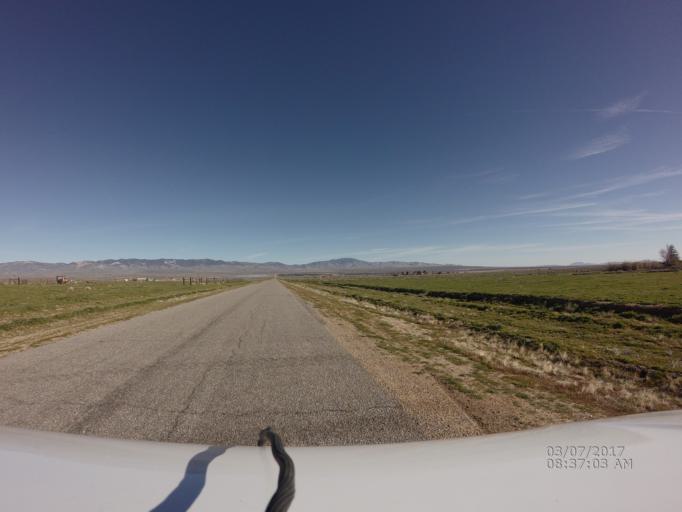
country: US
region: California
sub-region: Los Angeles County
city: Green Valley
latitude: 34.7896
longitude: -118.5457
